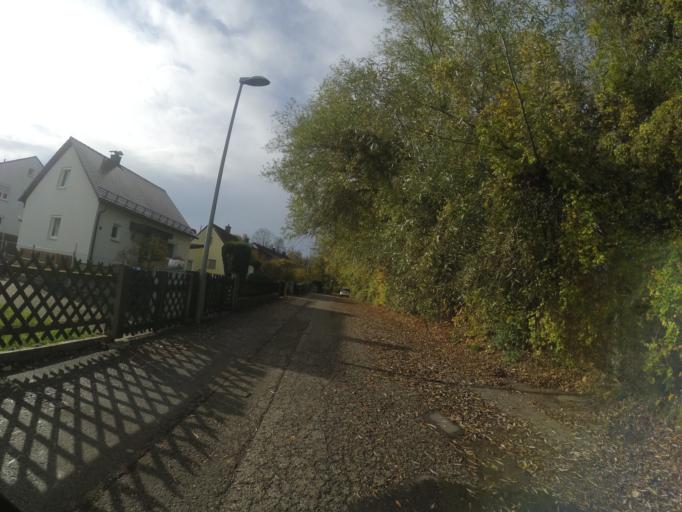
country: DE
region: Baden-Wuerttemberg
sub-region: Tuebingen Region
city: Ulm
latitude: 48.3641
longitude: 9.9863
